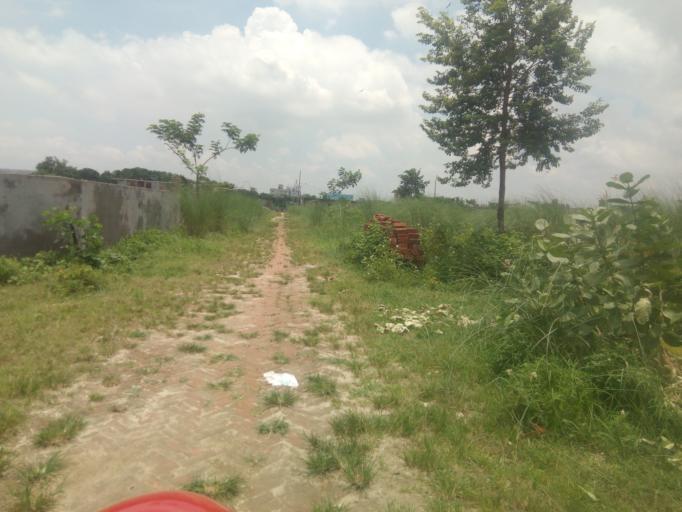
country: BD
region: Dhaka
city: Azimpur
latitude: 23.7557
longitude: 90.3451
